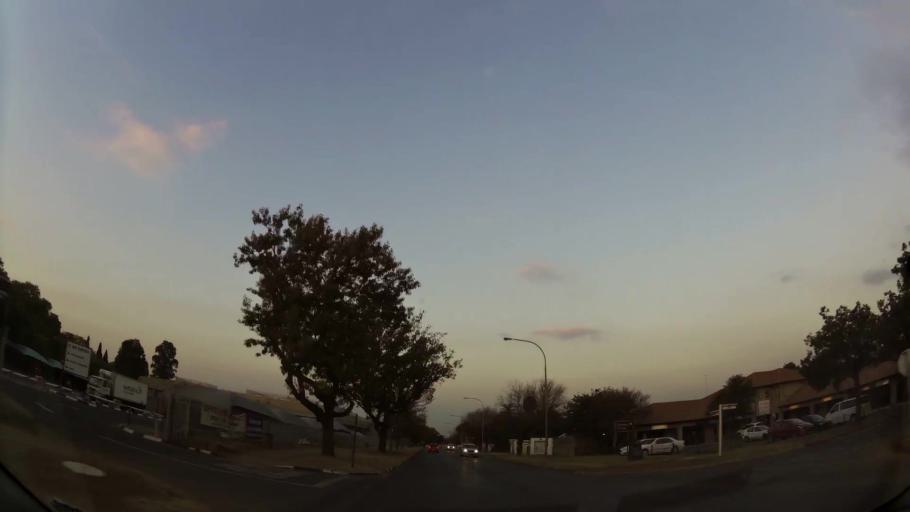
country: ZA
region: Gauteng
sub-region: Ekurhuleni Metropolitan Municipality
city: Benoni
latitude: -26.1638
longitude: 28.3210
